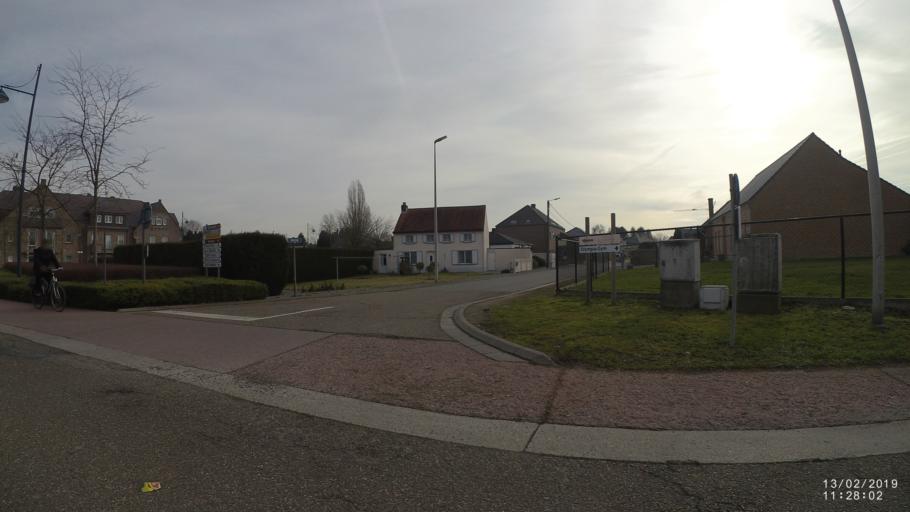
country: BE
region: Flanders
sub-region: Provincie Limburg
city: Halen
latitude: 50.9465
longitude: 5.1076
